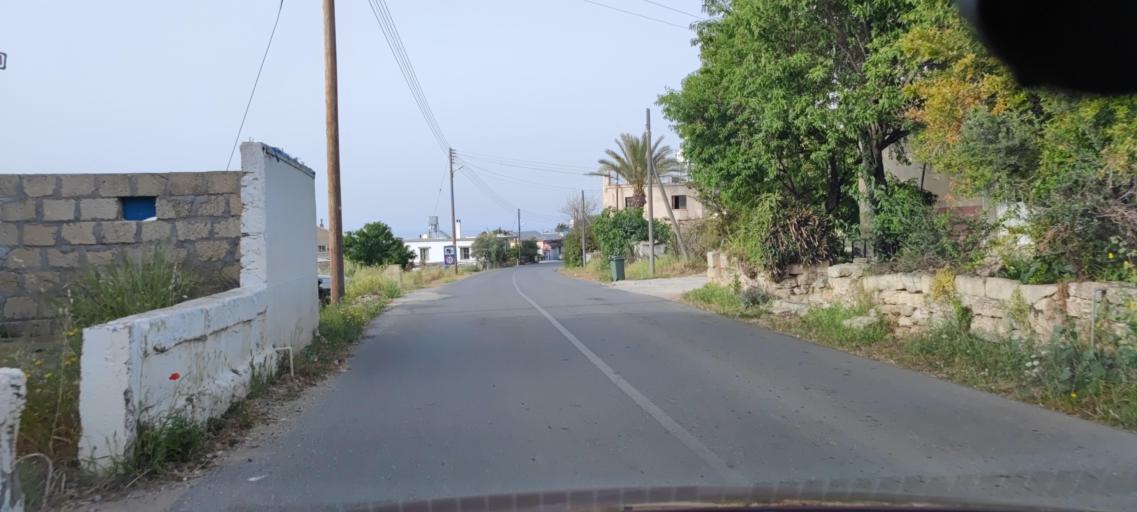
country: CY
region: Ammochostos
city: Leonarisso
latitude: 35.5395
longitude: 34.1938
